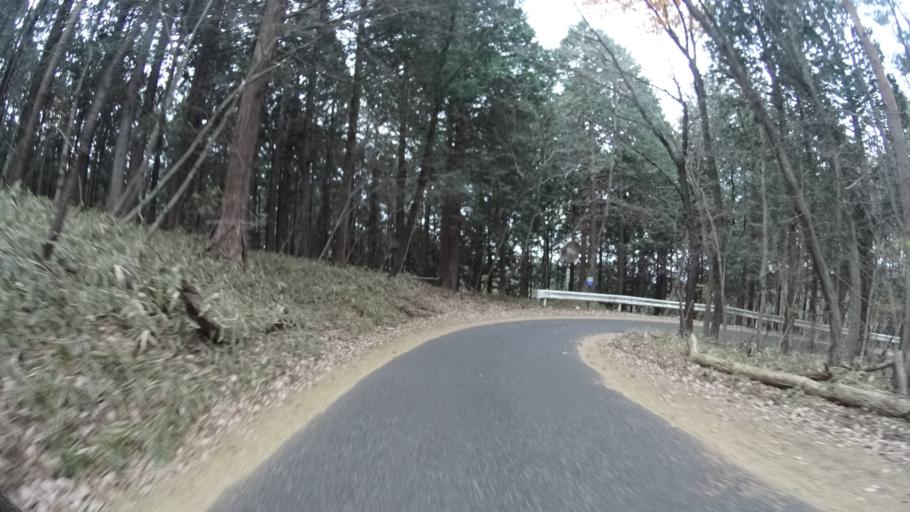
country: JP
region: Gunma
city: Omamacho-omama
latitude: 36.5049
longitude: 139.1833
